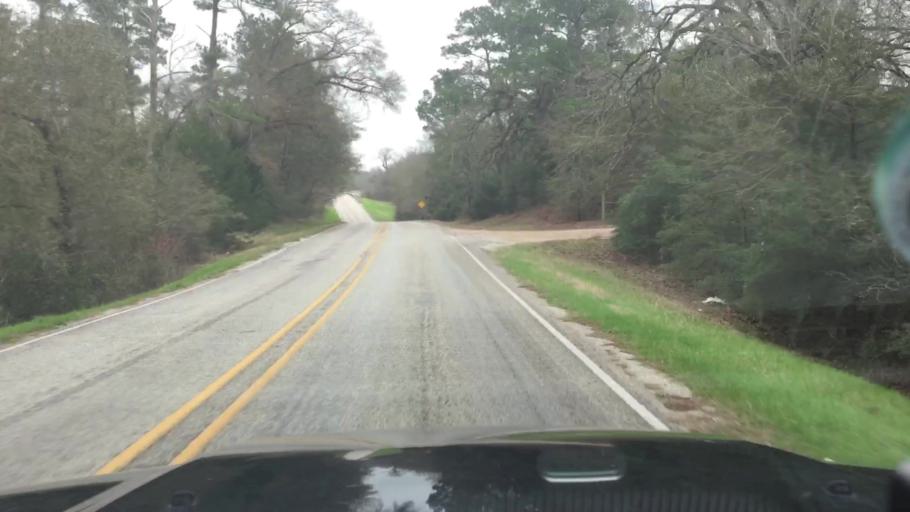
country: US
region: Texas
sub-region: Fayette County
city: La Grange
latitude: 30.0119
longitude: -96.9204
